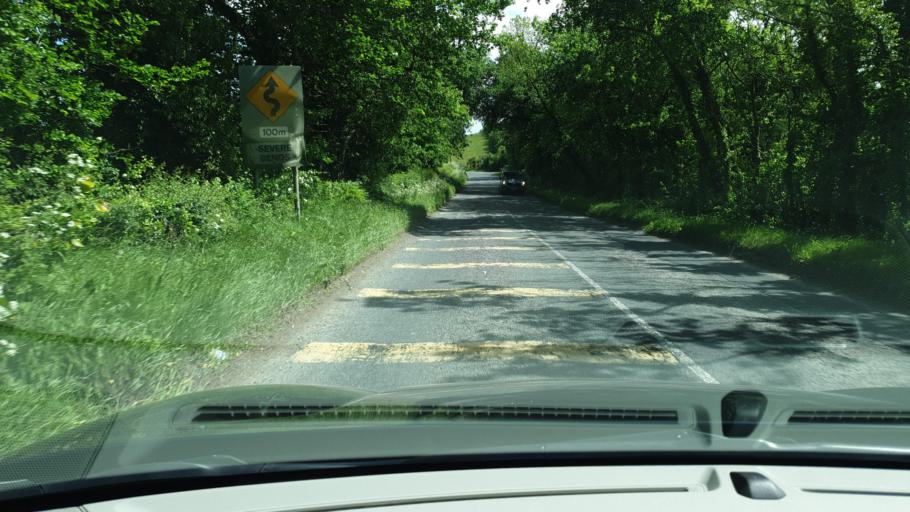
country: IE
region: Ulster
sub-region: An Cabhan
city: Kingscourt
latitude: 53.8321
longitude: -6.7621
